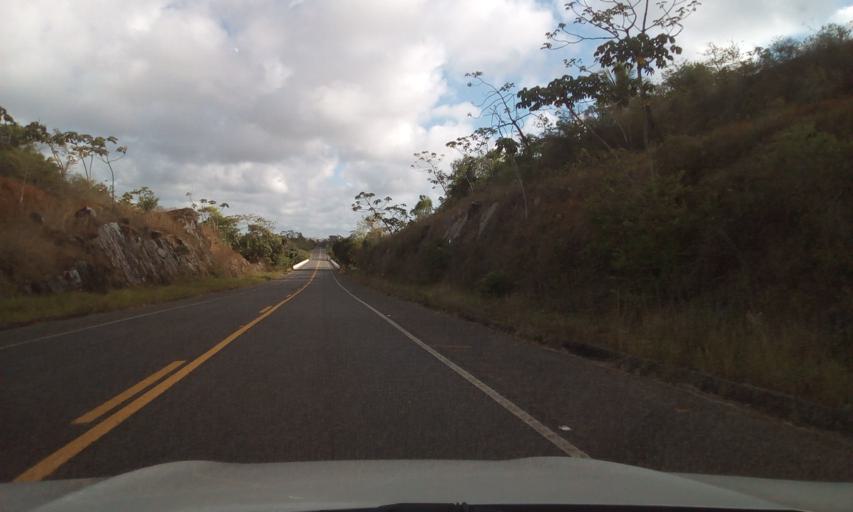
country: BR
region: Bahia
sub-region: Conde
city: Conde
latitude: -11.8091
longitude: -37.6321
